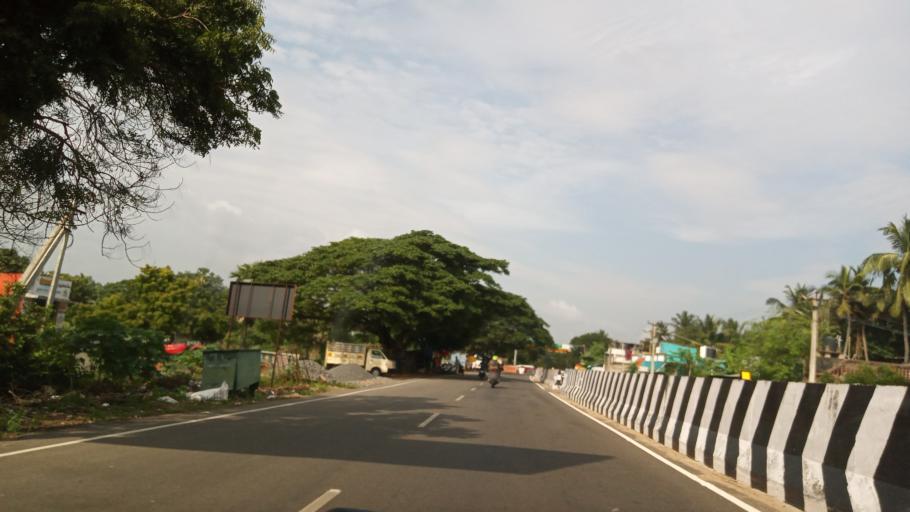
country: IN
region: Tamil Nadu
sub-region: Villupuram
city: Auroville
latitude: 12.0550
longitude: 79.8736
